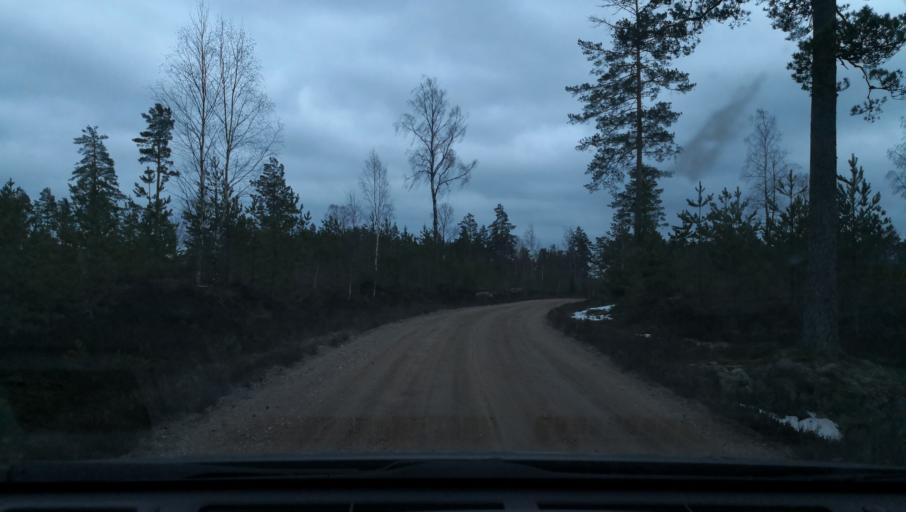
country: SE
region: OErebro
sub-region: Lindesbergs Kommun
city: Fellingsbro
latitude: 59.6046
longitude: 15.5781
